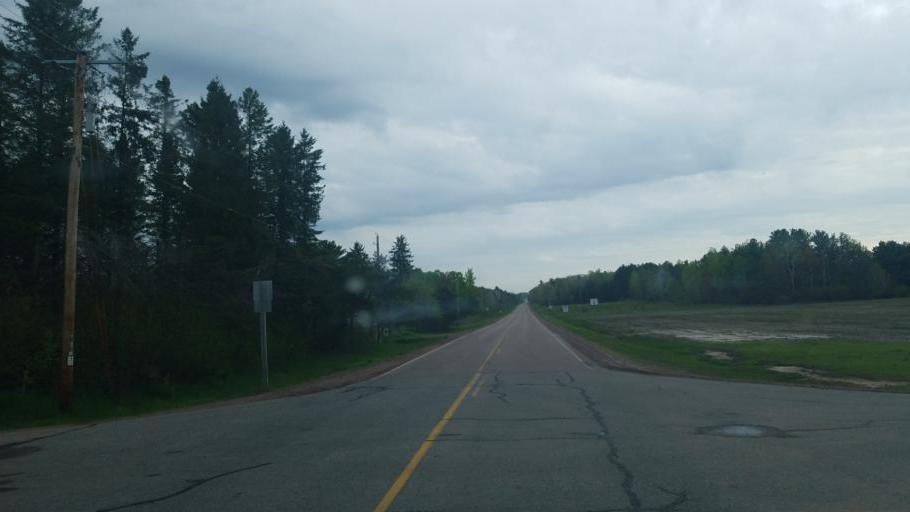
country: US
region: Wisconsin
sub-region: Wood County
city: Marshfield
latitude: 44.5557
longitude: -90.3000
